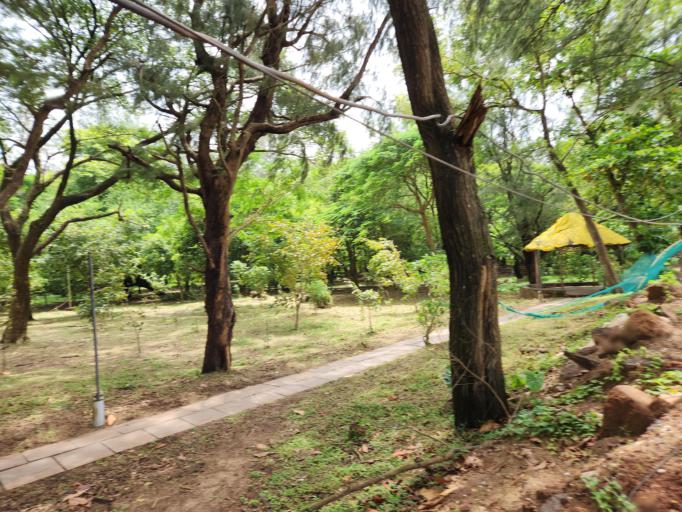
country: IN
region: Goa
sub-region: North Goa
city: Panaji
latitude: 15.4991
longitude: 73.8183
